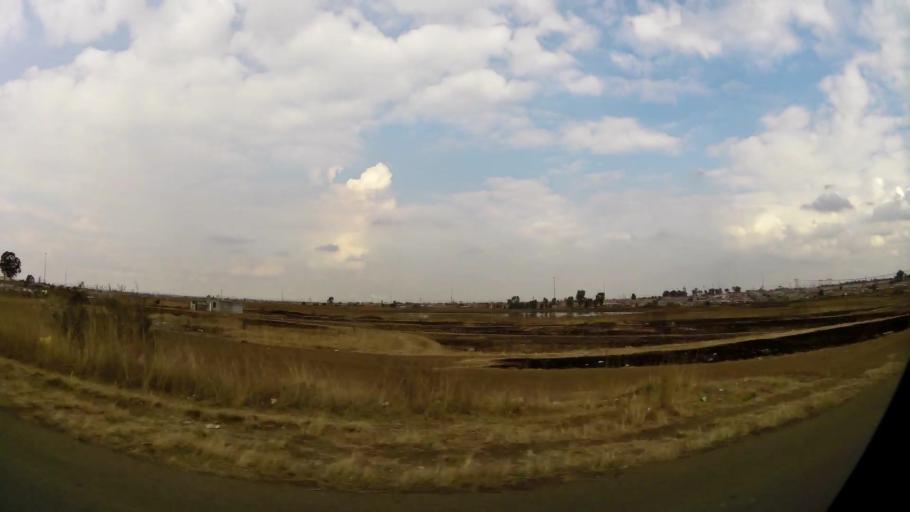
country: ZA
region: Gauteng
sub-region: Sedibeng District Municipality
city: Vanderbijlpark
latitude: -26.6696
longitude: 27.8621
